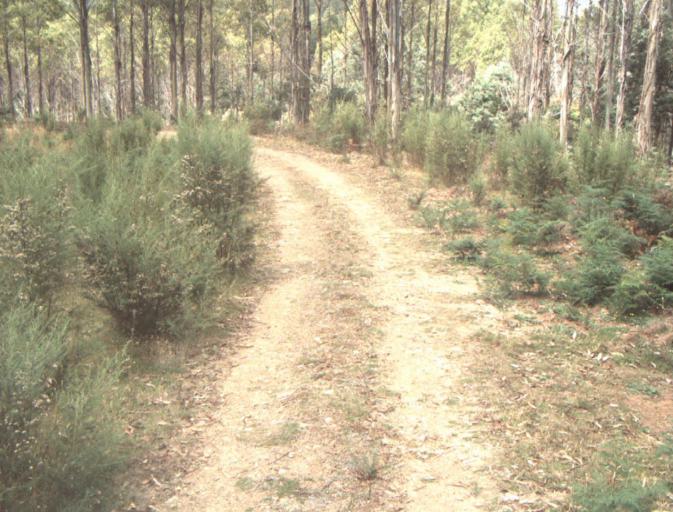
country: AU
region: Tasmania
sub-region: Dorset
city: Scottsdale
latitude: -41.4075
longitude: 147.5288
